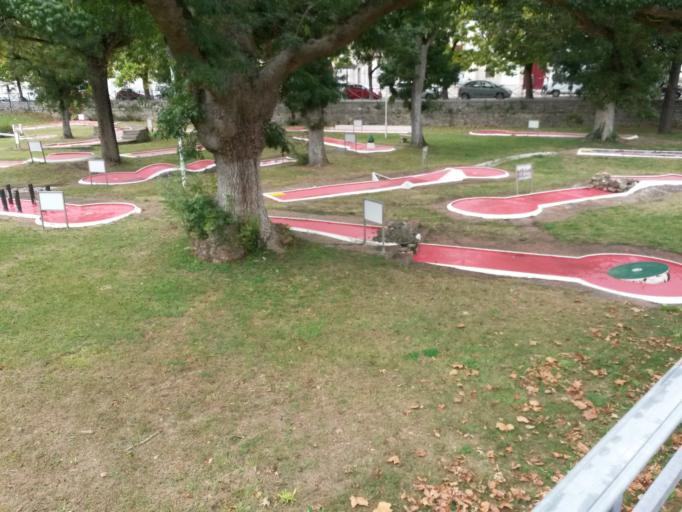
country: FR
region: Poitou-Charentes
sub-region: Departement de la Charente-Maritime
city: Saint-Trojan-les-Bains
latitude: 45.8857
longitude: -1.1941
